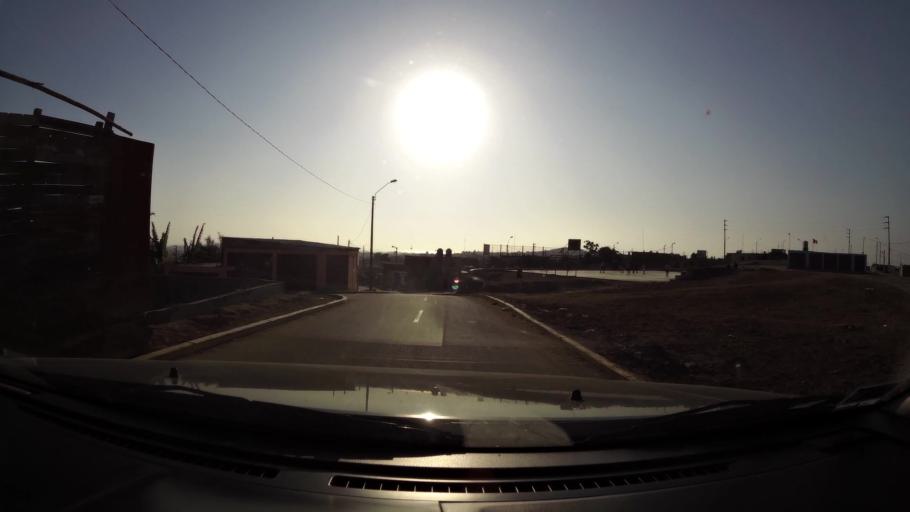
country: PE
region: Ica
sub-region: Provincia de Pisco
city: Villa Tupac Amaru
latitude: -13.7076
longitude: -76.1465
